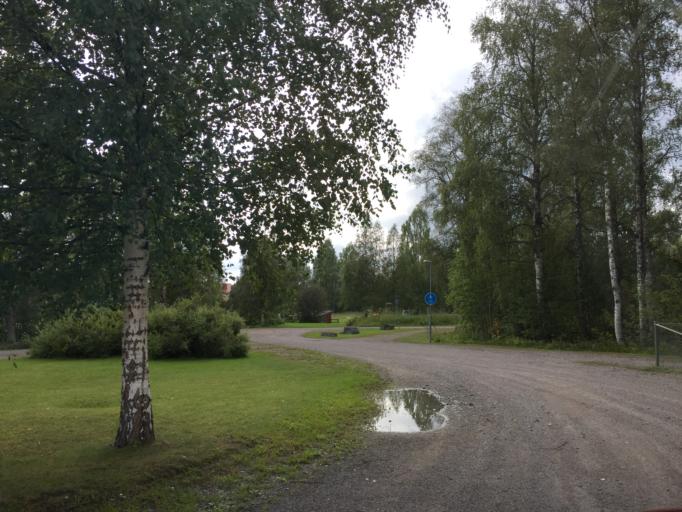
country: SE
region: Gaevleborg
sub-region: Ljusdals Kommun
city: Jaervsoe
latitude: 61.7951
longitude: 16.2075
